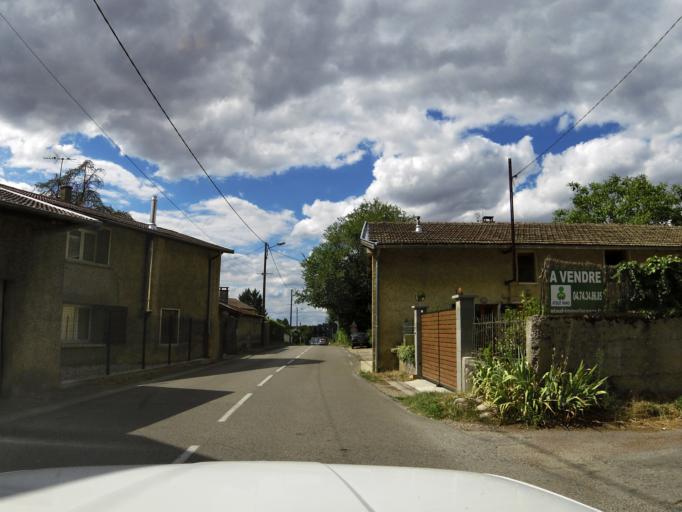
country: FR
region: Rhone-Alpes
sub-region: Departement de l'Ain
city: Chazey-sur-Ain
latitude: 45.8727
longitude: 5.2228
